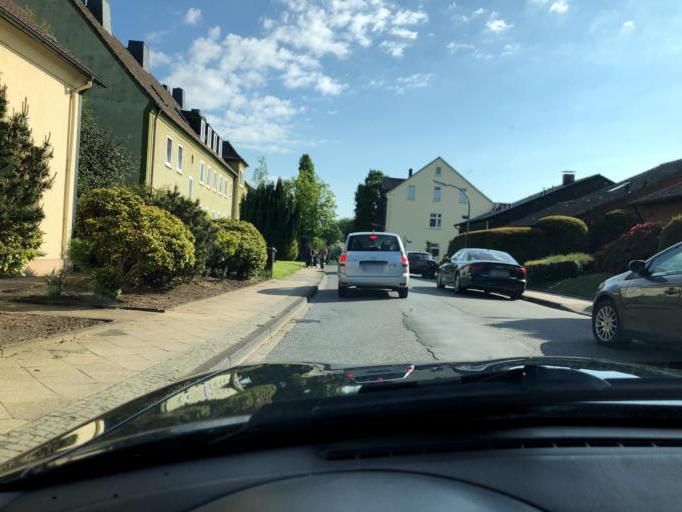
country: DE
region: North Rhine-Westphalia
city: Bochum-Hordel
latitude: 51.4578
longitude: 7.1560
